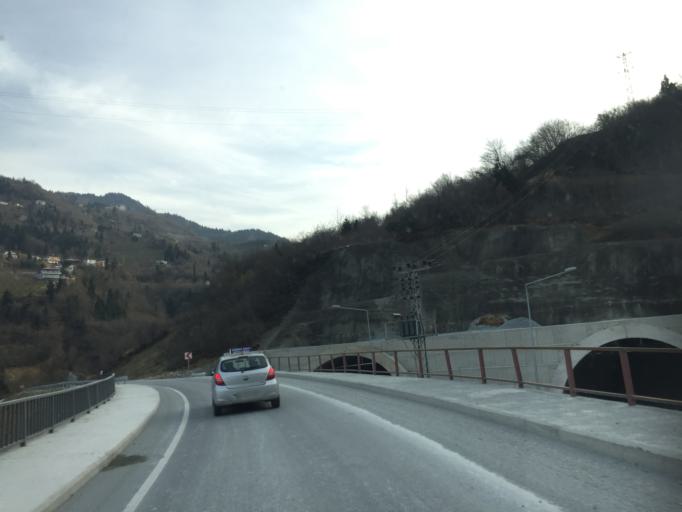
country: TR
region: Trabzon
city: Macka
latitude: 40.8285
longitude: 39.6206
